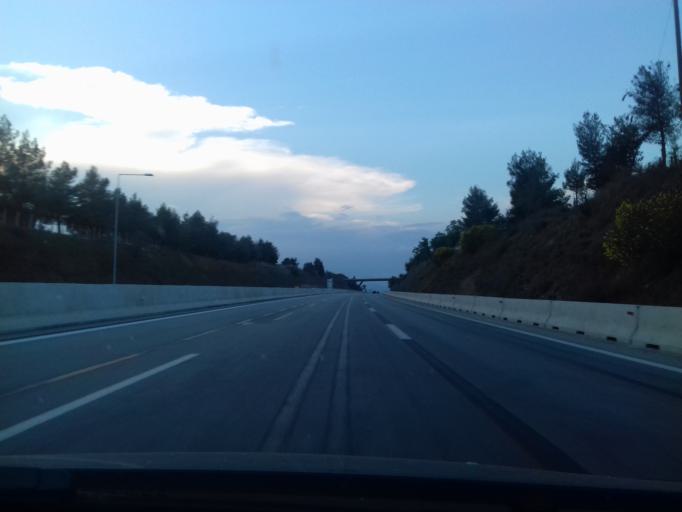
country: GR
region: West Greece
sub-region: Nomos Achaias
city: Aigio
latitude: 38.2385
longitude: 22.0766
